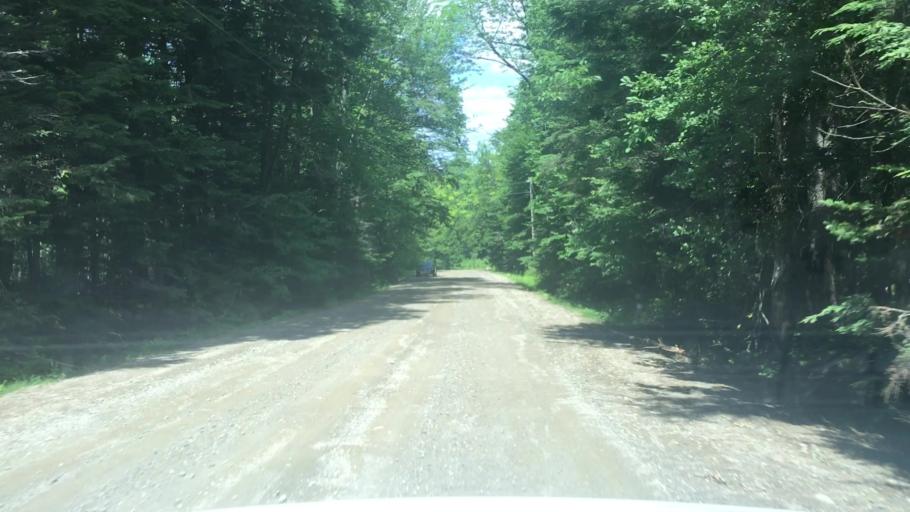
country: US
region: Maine
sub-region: Waldo County
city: Searsmont
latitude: 44.4736
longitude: -69.2976
